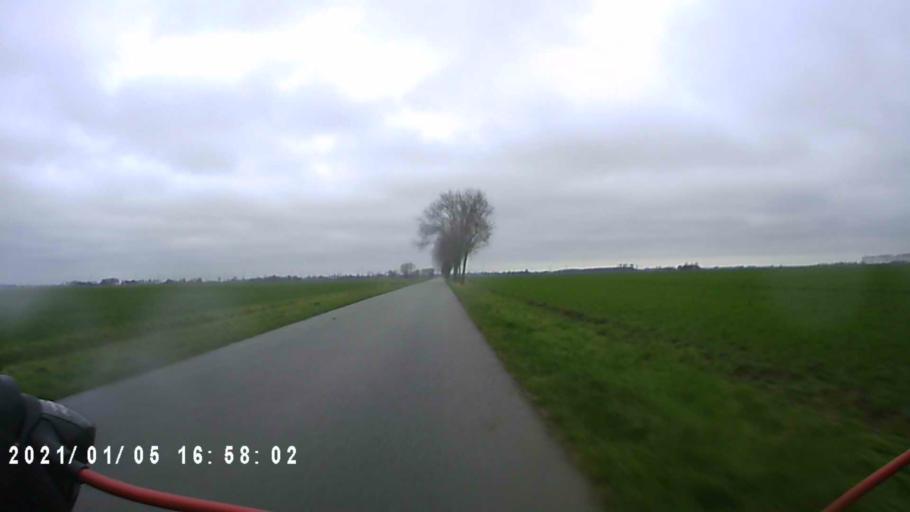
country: NL
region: Groningen
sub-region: Gemeente  Oldambt
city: Winschoten
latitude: 53.2482
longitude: 7.0563
